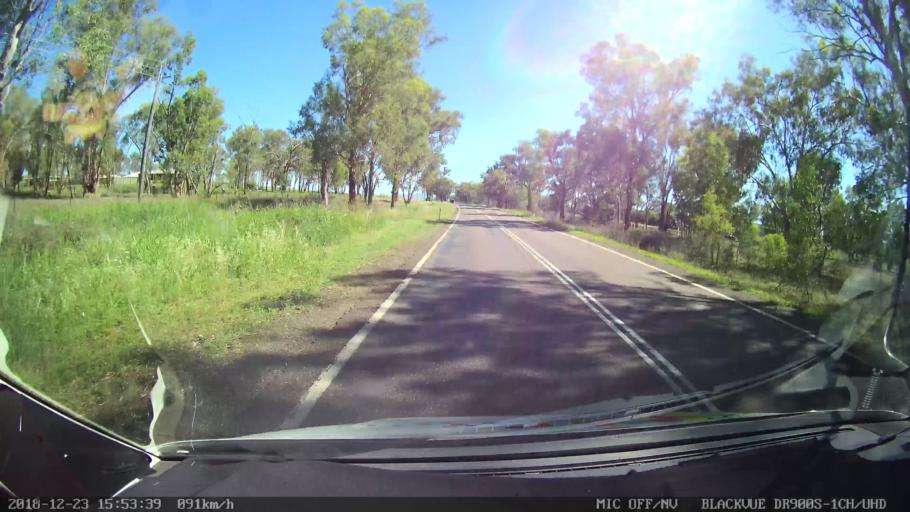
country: AU
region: New South Wales
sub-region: Tamworth Municipality
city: Phillip
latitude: -31.1359
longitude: 150.8797
